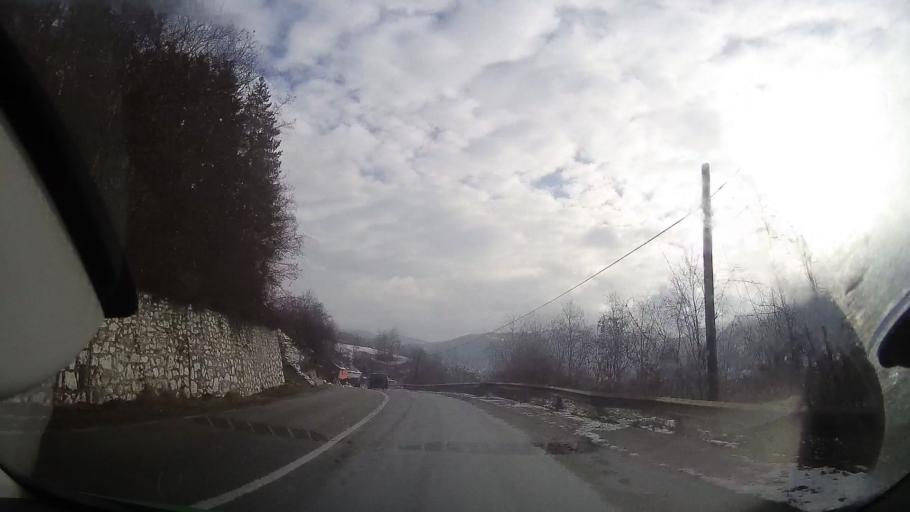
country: RO
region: Alba
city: Salciua de Sus
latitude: 46.3953
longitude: 23.3863
